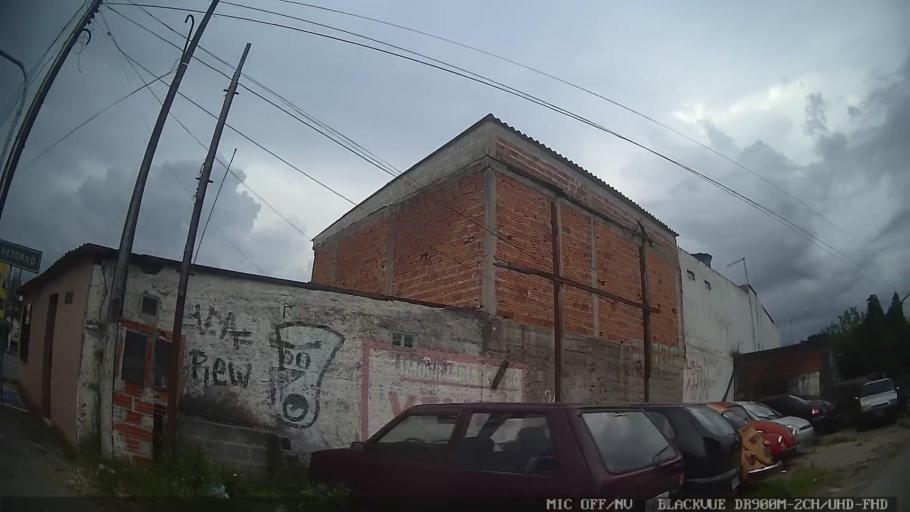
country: BR
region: Sao Paulo
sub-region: Suzano
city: Suzano
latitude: -23.5416
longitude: -46.3040
